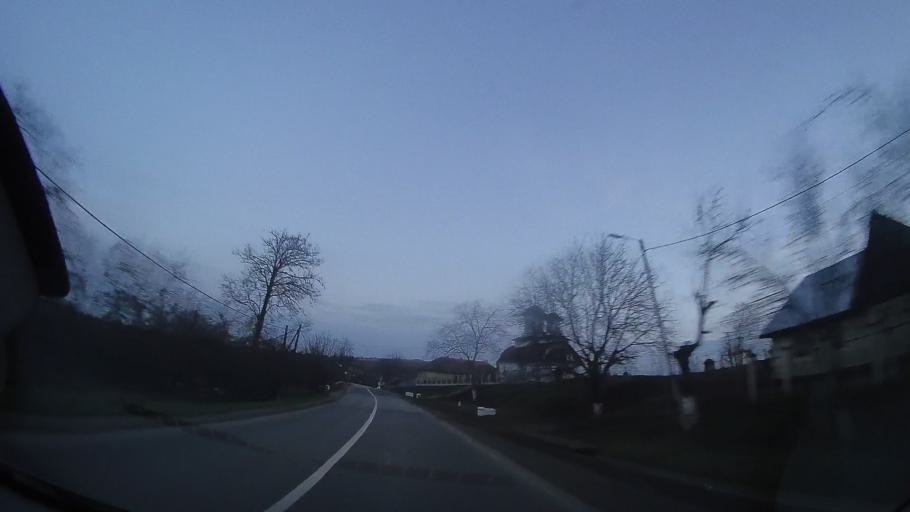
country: RO
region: Cluj
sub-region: Comuna Mociu
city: Mociu
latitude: 46.7914
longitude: 24.0719
